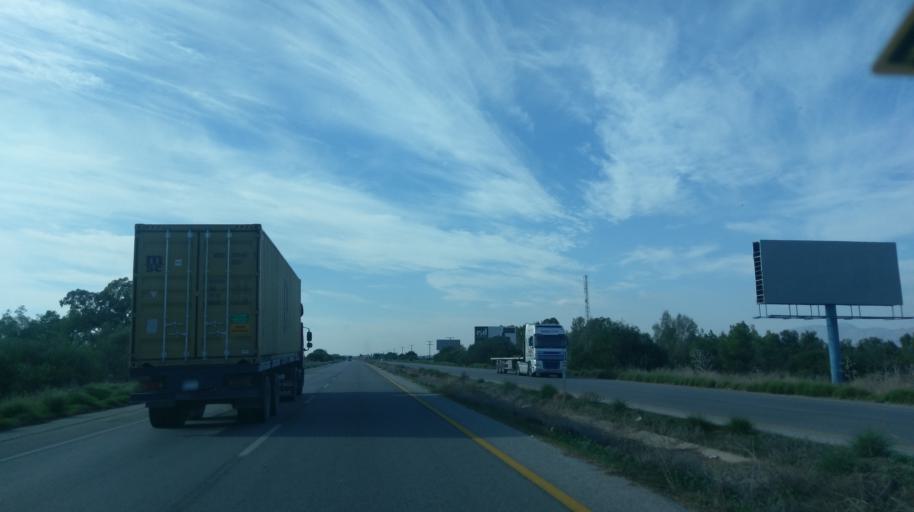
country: CY
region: Ammochostos
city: Lefkonoiko
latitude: 35.1860
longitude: 33.6546
